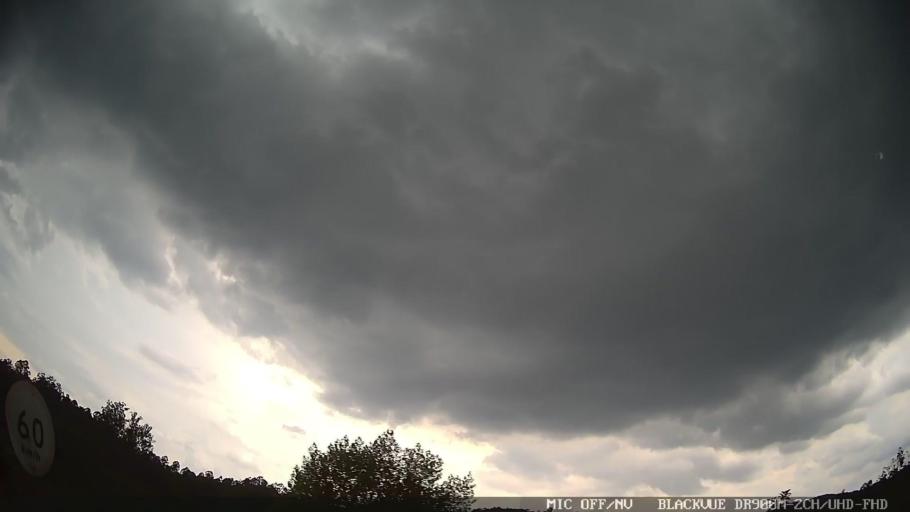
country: BR
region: Sao Paulo
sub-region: Itatiba
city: Itatiba
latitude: -23.0072
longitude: -46.8998
